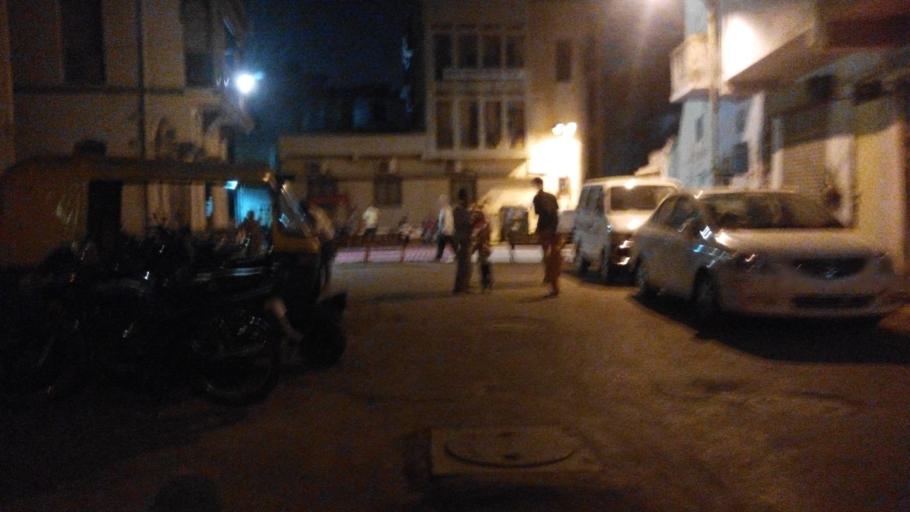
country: IN
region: Gujarat
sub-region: Ahmadabad
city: Ahmedabad
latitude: 23.0350
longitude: 72.5922
